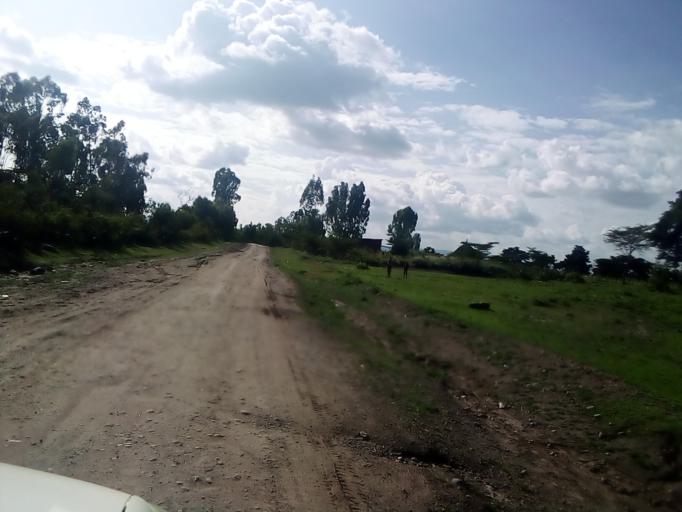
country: ET
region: Southern Nations, Nationalities, and People's Region
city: K'olito
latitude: 7.6407
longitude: 38.0573
